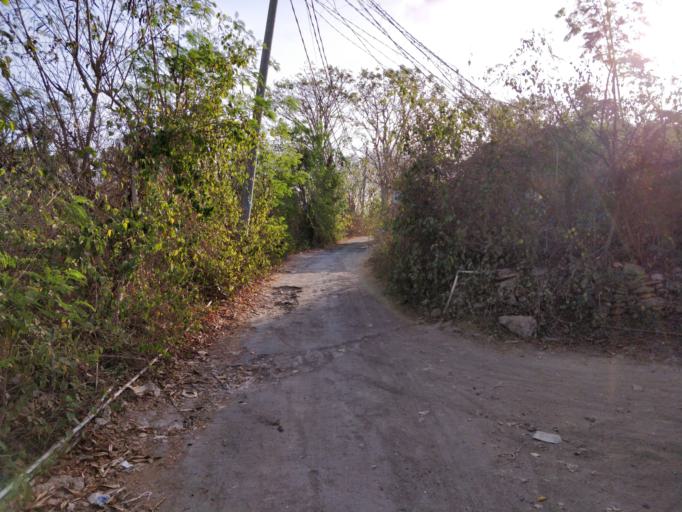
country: ID
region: Bali
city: Lembongan Kawan
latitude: -8.6841
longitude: 115.4313
